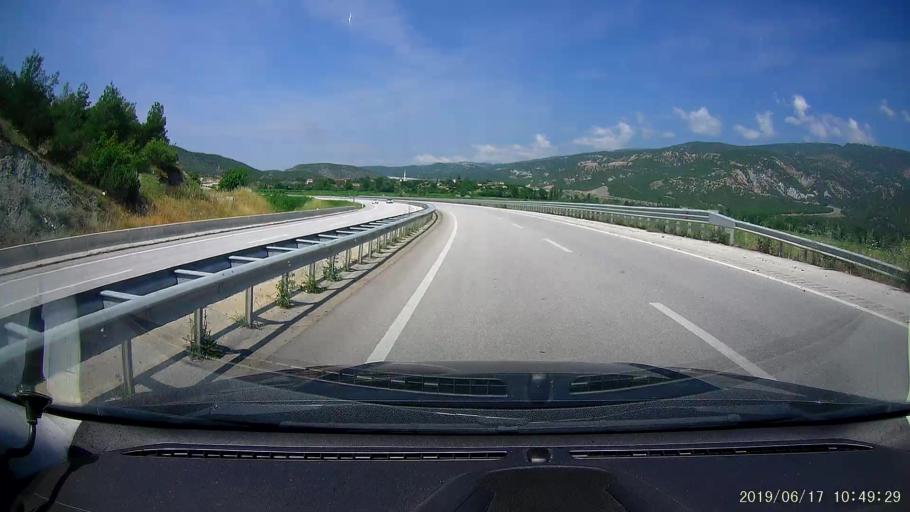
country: TR
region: Corum
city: Hacihamza
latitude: 41.1020
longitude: 34.4087
